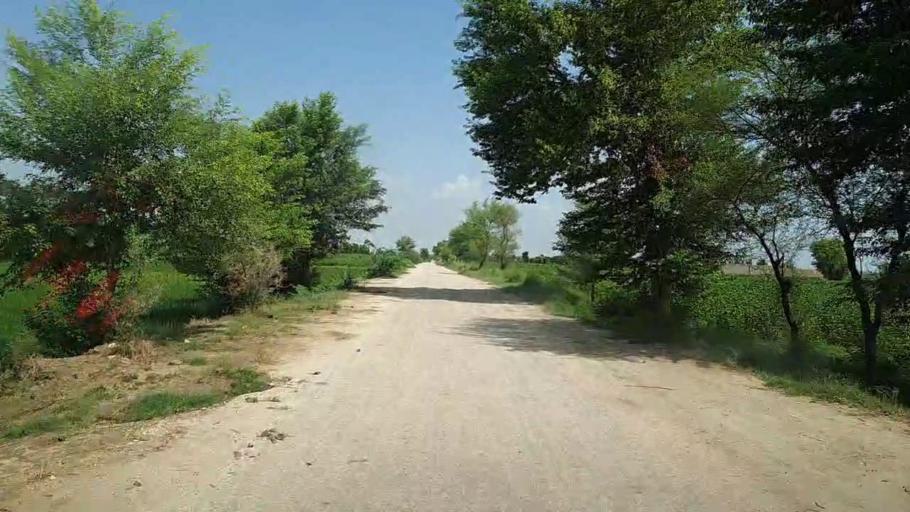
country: PK
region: Sindh
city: Bhiria
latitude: 26.8749
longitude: 68.2494
